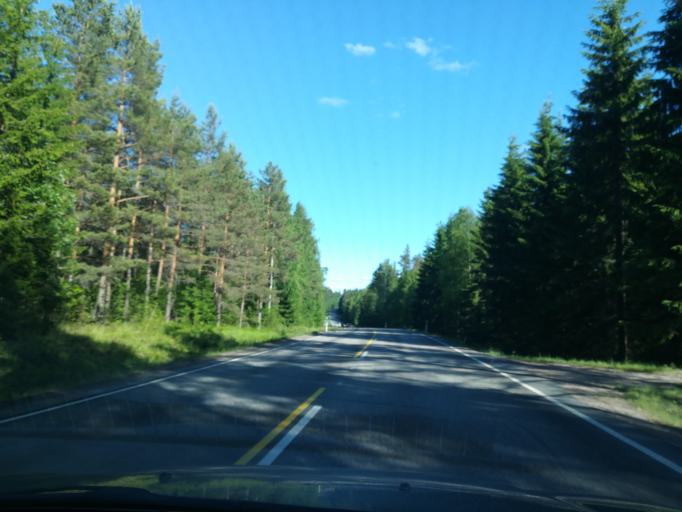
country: FI
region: South Karelia
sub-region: Imatra
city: Ruokolahti
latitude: 61.3594
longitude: 28.7053
